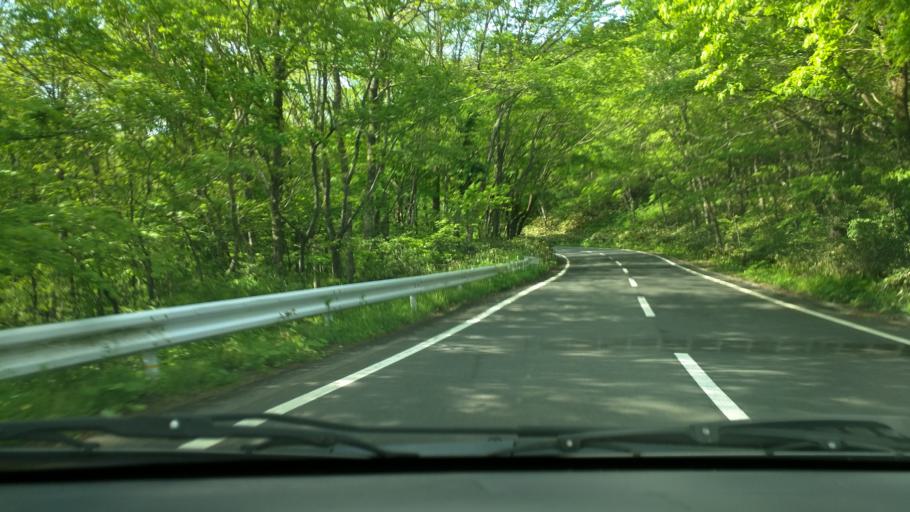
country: JP
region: Tochigi
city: Kuroiso
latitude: 37.2371
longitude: 140.0717
